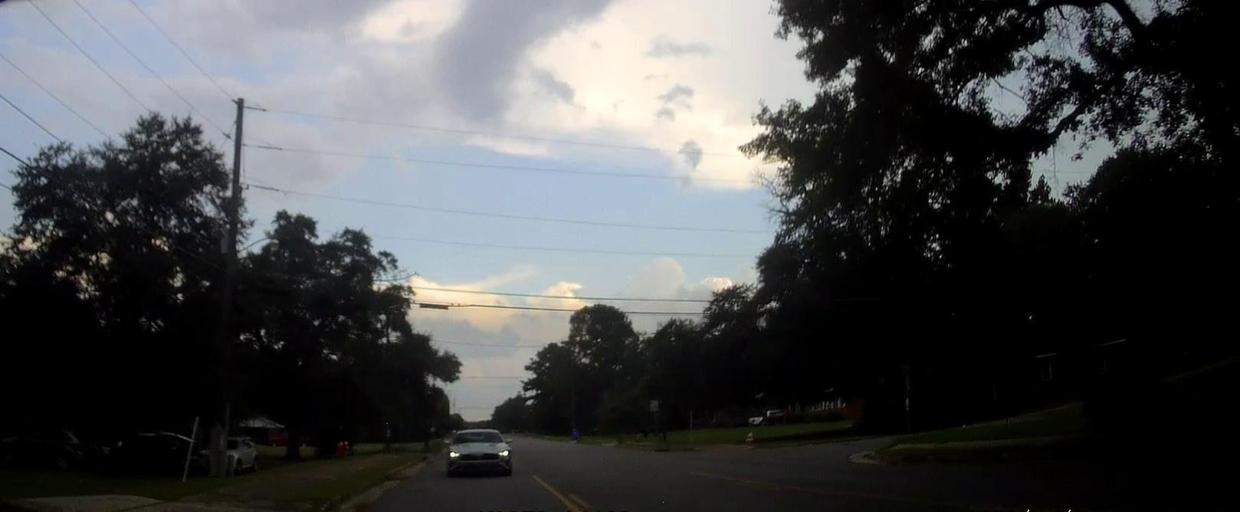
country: US
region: Georgia
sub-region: Laurens County
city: Dublin
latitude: 32.5664
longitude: -82.9113
